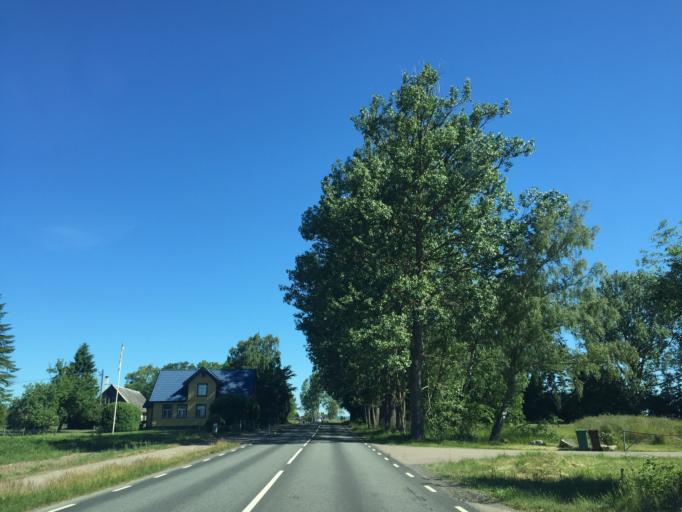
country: SE
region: Skane
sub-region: Angelholms Kommun
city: AEngelholm
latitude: 56.1973
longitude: 12.8527
